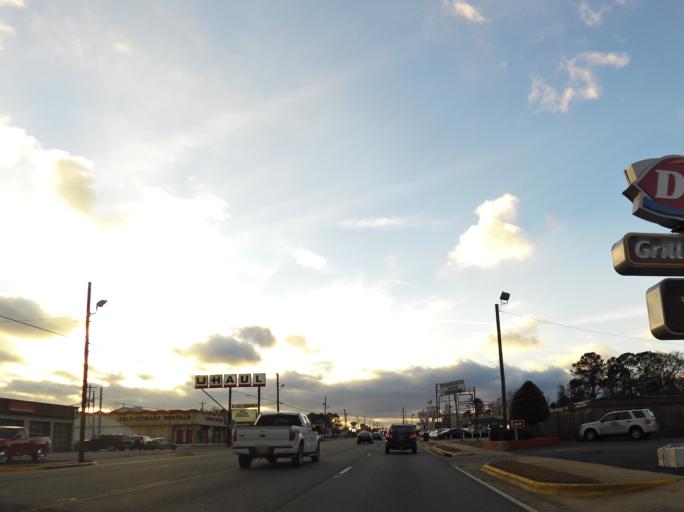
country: US
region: Georgia
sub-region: Houston County
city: Warner Robins
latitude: 32.6183
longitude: -83.6172
